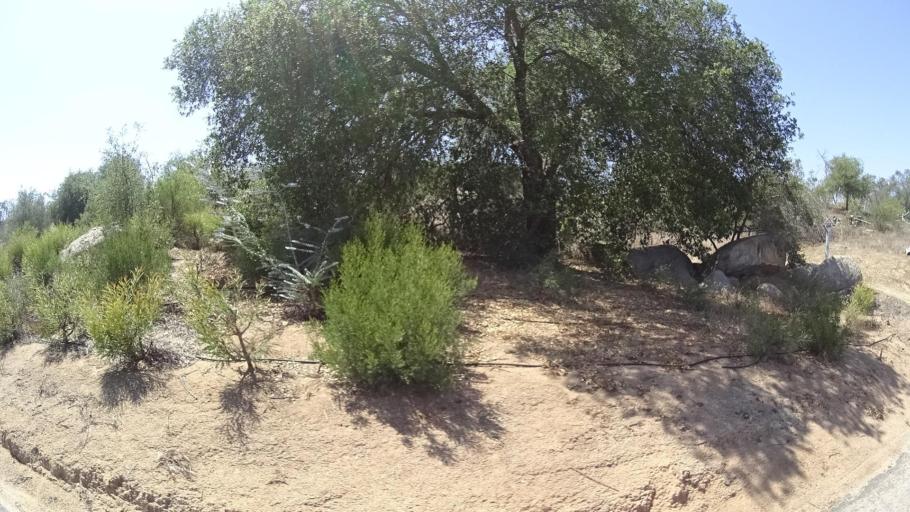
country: US
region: California
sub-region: San Diego County
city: Fallbrook
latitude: 33.4286
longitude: -117.2699
